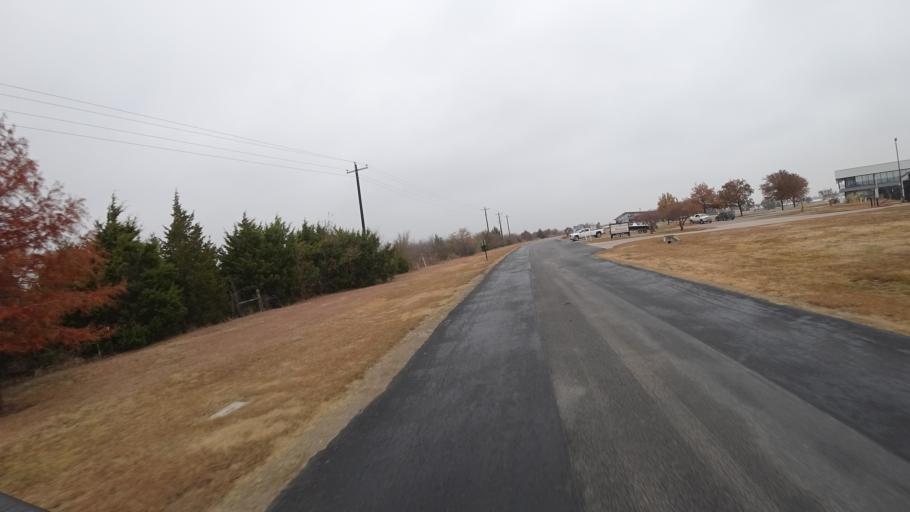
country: US
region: Texas
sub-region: Denton County
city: The Colony
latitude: 33.0710
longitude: -96.9197
